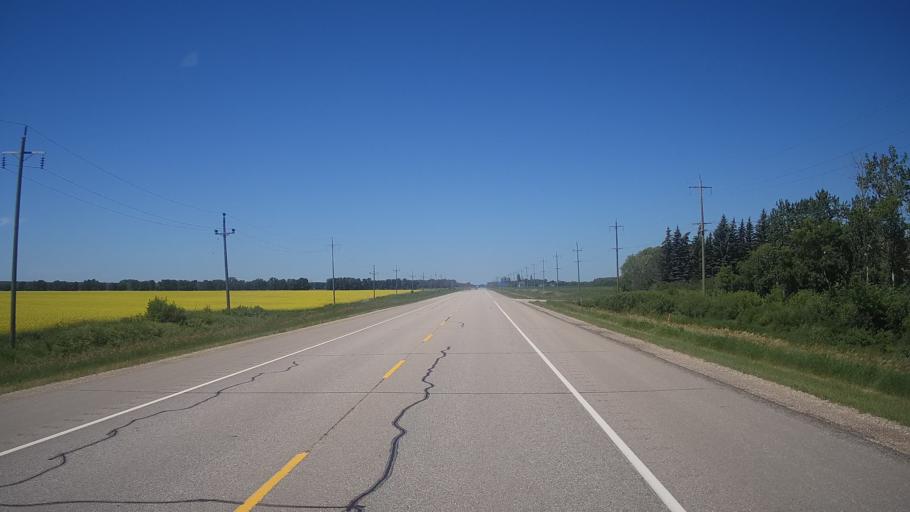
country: CA
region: Manitoba
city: Neepawa
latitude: 50.2253
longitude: -99.3197
